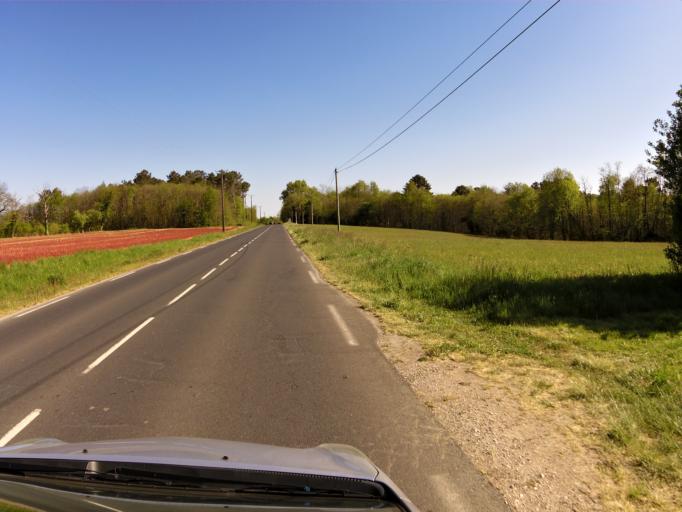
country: FR
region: Aquitaine
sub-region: Departement de la Dordogne
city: Montignac
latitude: 45.0155
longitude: 1.2374
